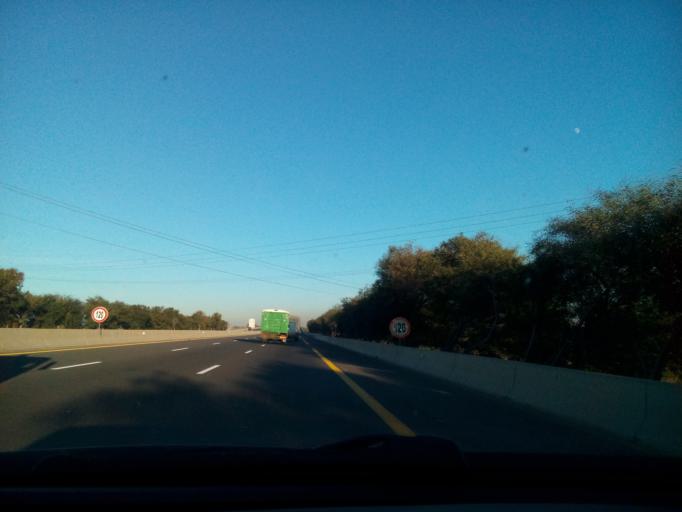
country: DZ
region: Relizane
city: Djidiouia
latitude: 35.9254
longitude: 0.7866
